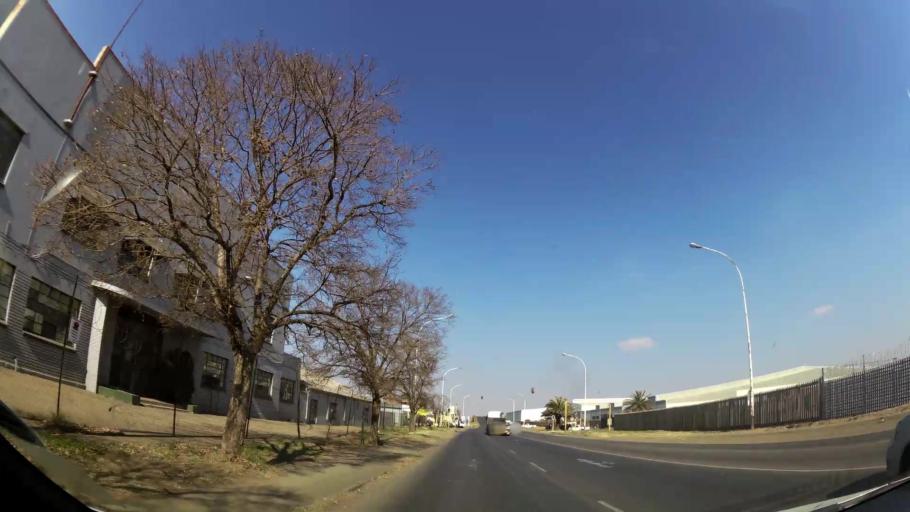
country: ZA
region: Gauteng
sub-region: Ekurhuleni Metropolitan Municipality
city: Boksburg
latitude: -26.2271
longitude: 28.2928
